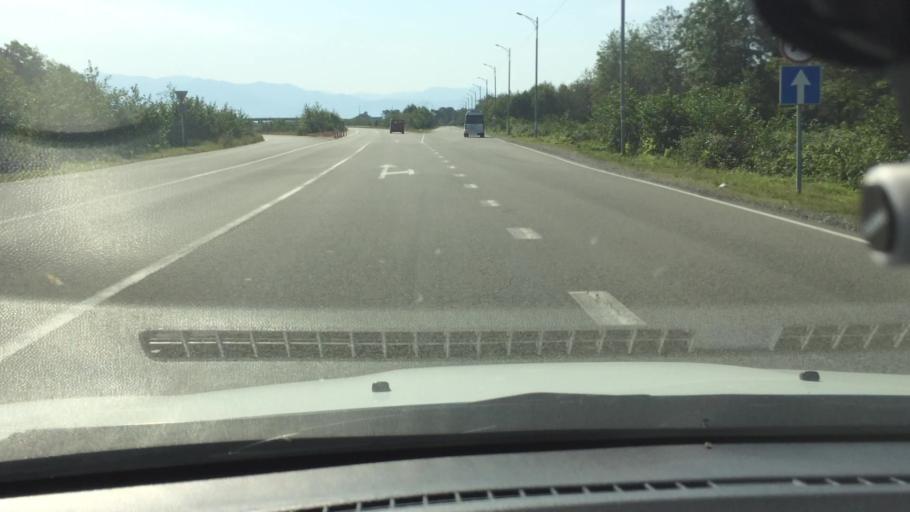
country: GE
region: Guria
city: Urek'i
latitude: 41.9246
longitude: 41.7735
